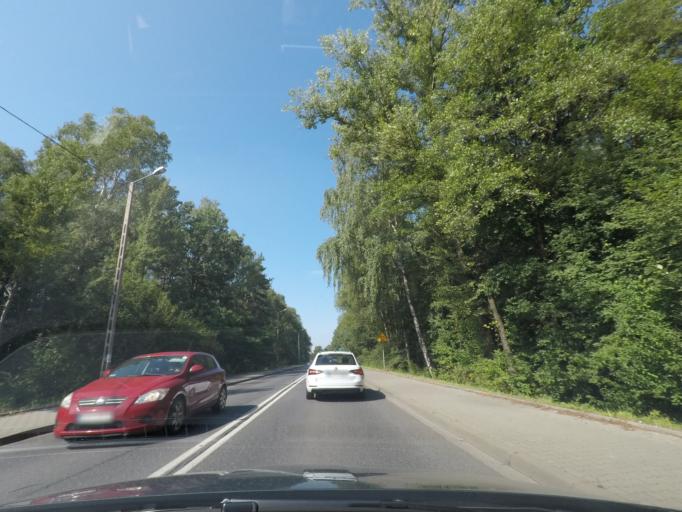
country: PL
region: Lesser Poland Voivodeship
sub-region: Powiat chrzanowski
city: Chrzanow
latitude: 50.1315
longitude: 19.3762
